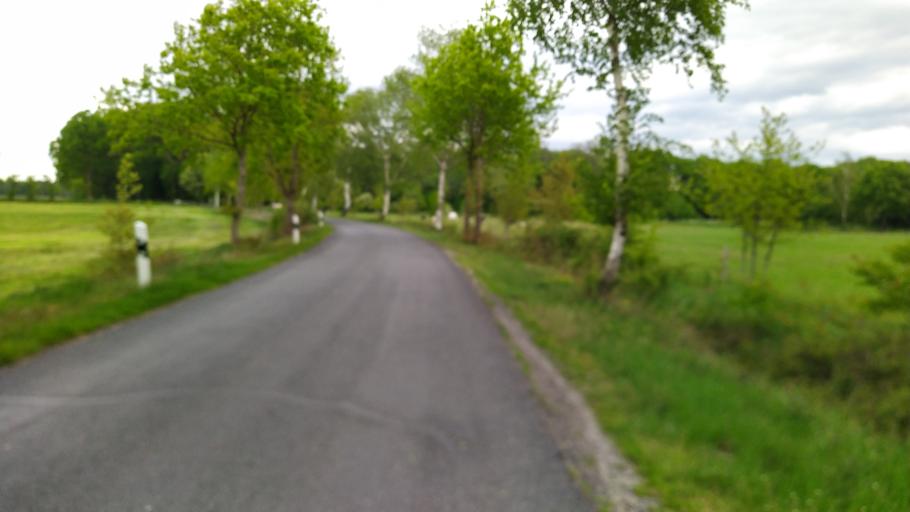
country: DE
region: Lower Saxony
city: Farven
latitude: 53.4005
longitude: 9.3576
